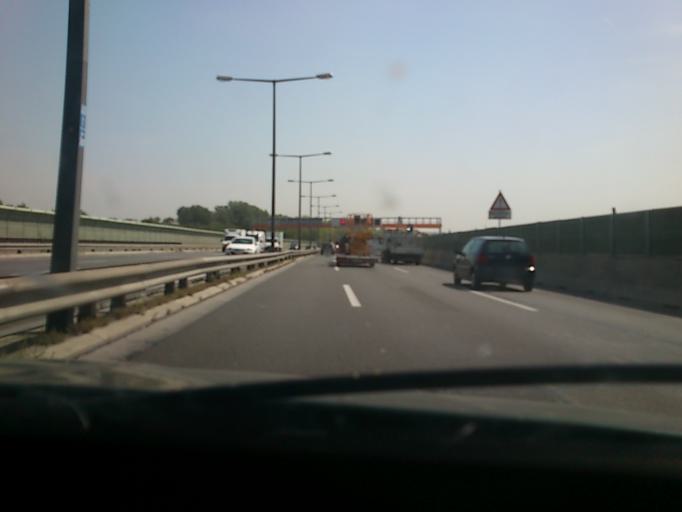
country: AT
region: Lower Austria
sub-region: Politischer Bezirk Modling
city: Vosendorf
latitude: 48.1527
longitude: 16.3533
